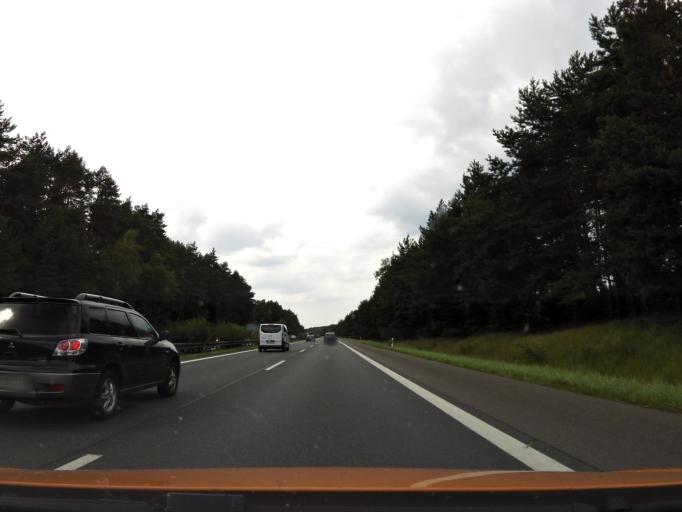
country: DE
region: Brandenburg
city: Birkenwerder
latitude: 52.6939
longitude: 13.3077
